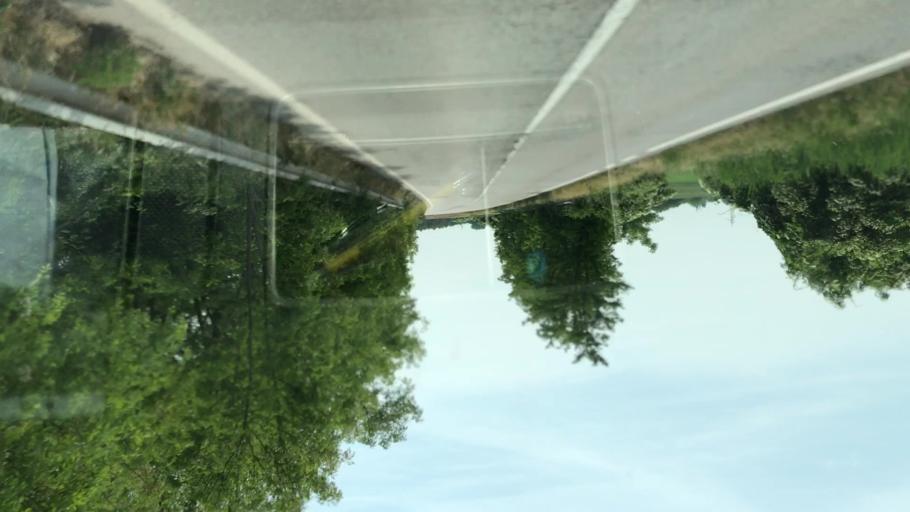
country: IT
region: Lombardy
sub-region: Provincia di Mantova
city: Gazzuolo
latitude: 45.0722
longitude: 10.5896
